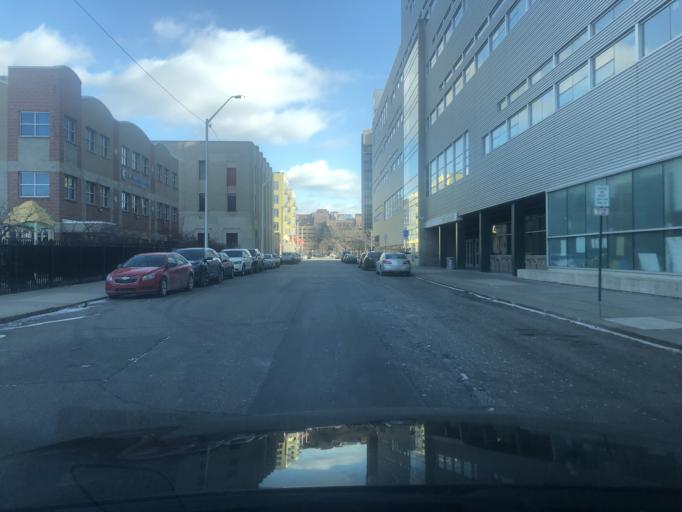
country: US
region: Michigan
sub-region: Wayne County
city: Detroit
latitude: 42.3487
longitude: -83.0615
